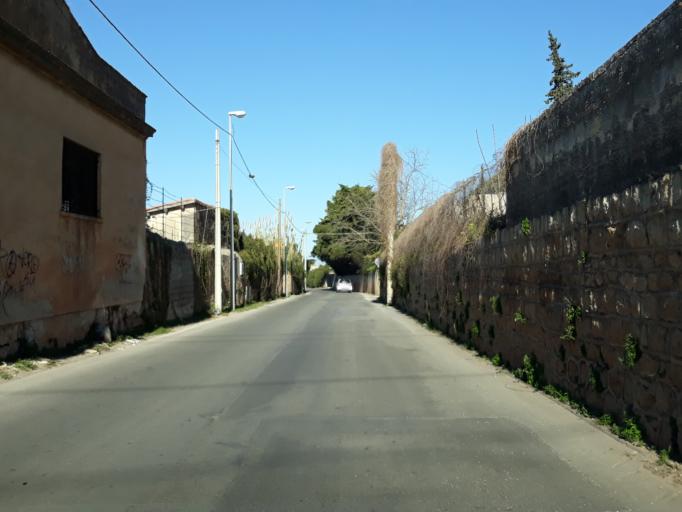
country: IT
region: Sicily
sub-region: Palermo
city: Ciaculli
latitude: 38.0855
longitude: 13.3794
